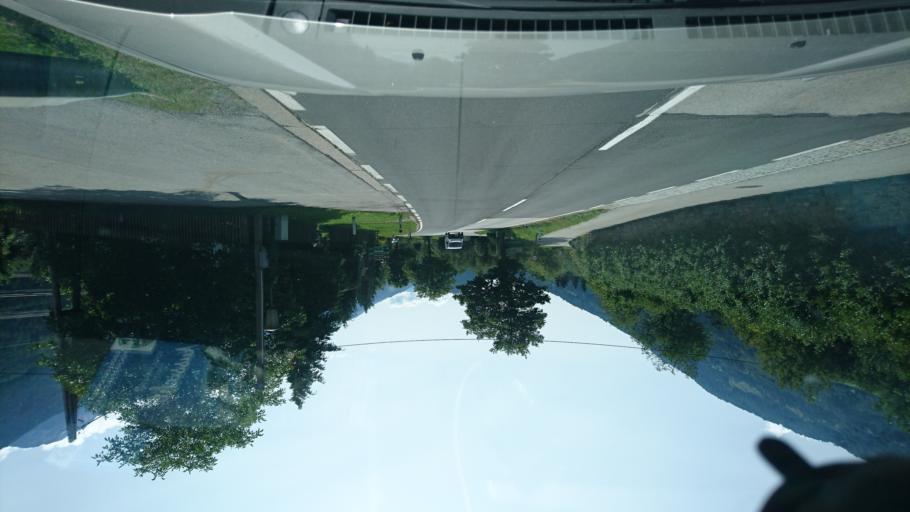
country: AT
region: Carinthia
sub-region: Politischer Bezirk Spittal an der Drau
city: Obervellach
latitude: 46.9150
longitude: 13.2400
